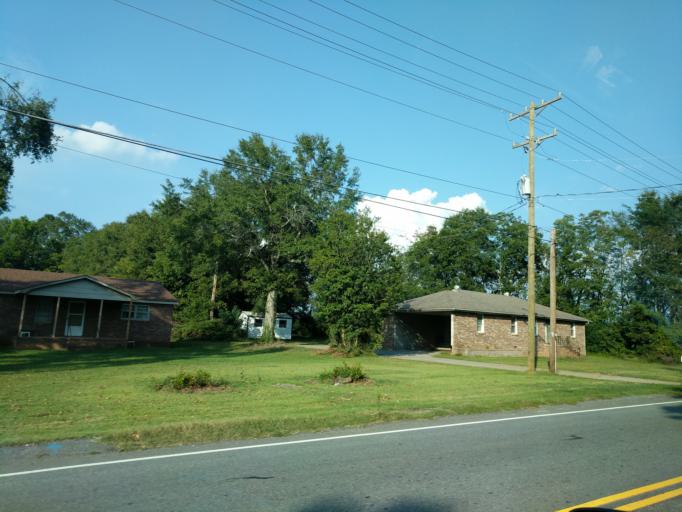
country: US
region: South Carolina
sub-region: Anderson County
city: Piedmont
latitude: 34.7086
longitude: -82.4946
